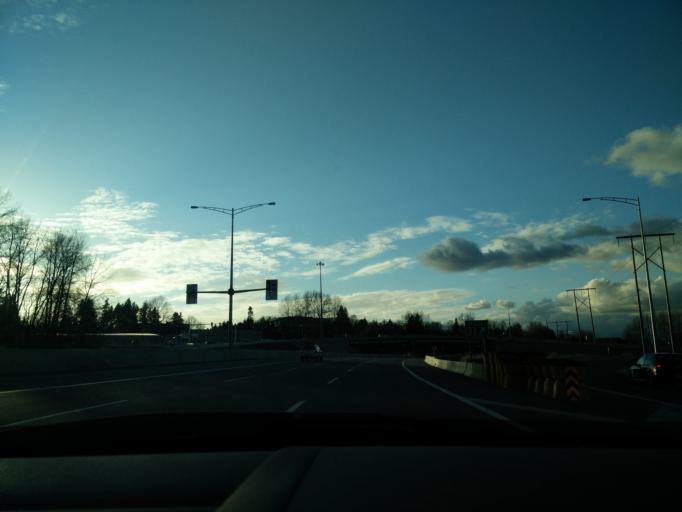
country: CA
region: British Columbia
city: Burnaby
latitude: 49.2424
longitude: -122.9646
